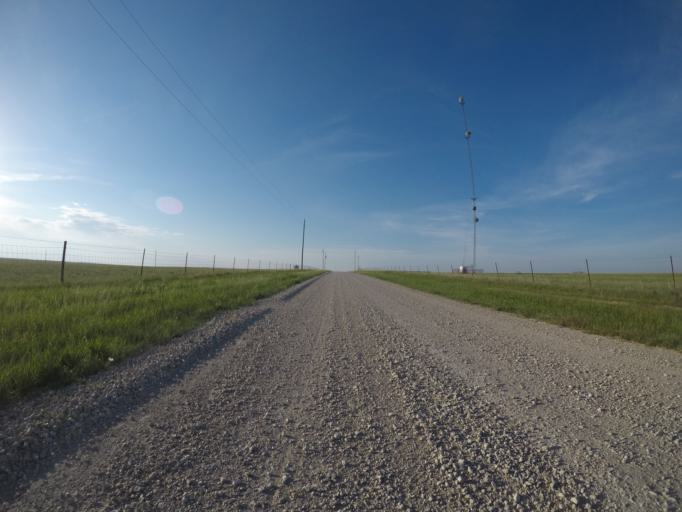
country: US
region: Kansas
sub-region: Riley County
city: Manhattan
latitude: 39.0276
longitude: -96.4918
